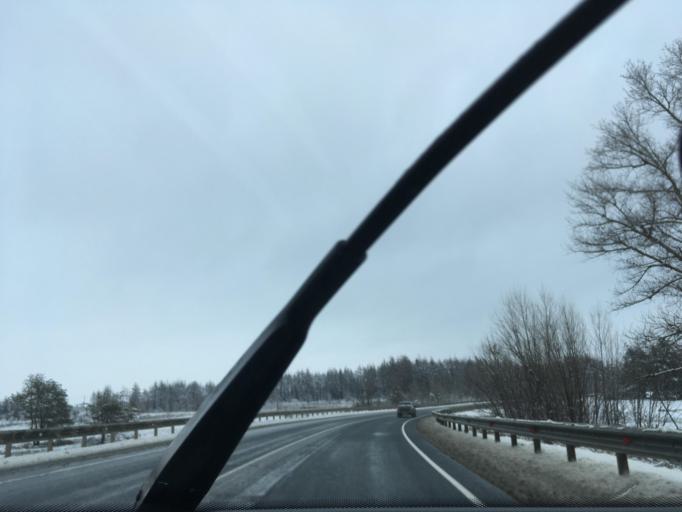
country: RU
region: Voronezj
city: Zabolotovka
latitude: 50.2450
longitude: 39.3823
